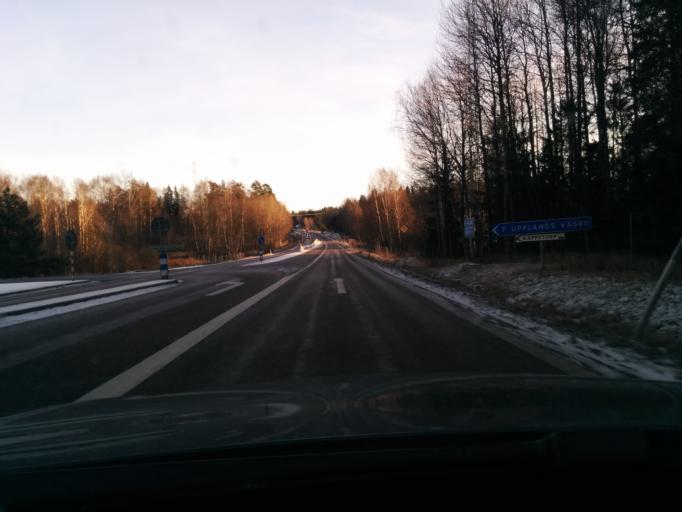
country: SE
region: Stockholm
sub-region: Jarfalla Kommun
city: Jakobsberg
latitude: 59.4766
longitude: 17.8526
